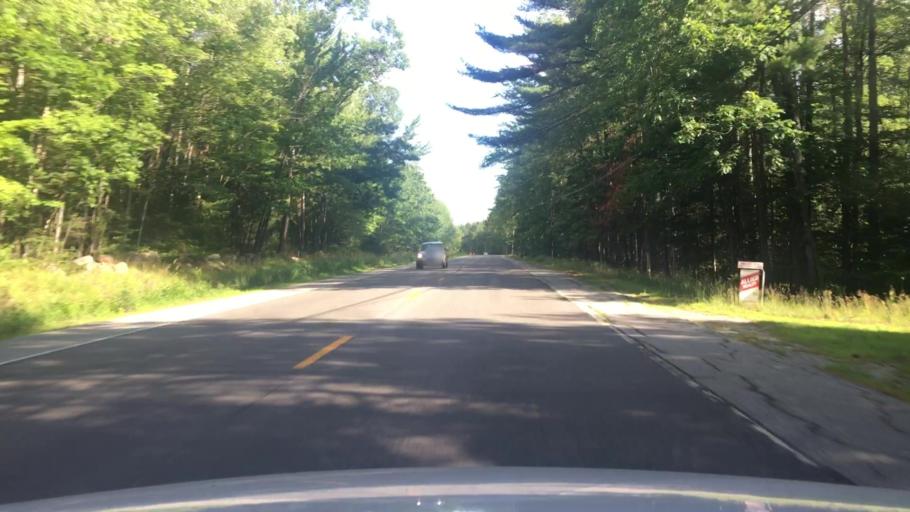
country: US
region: Maine
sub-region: Franklin County
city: Jay
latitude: 44.5360
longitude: -70.2337
